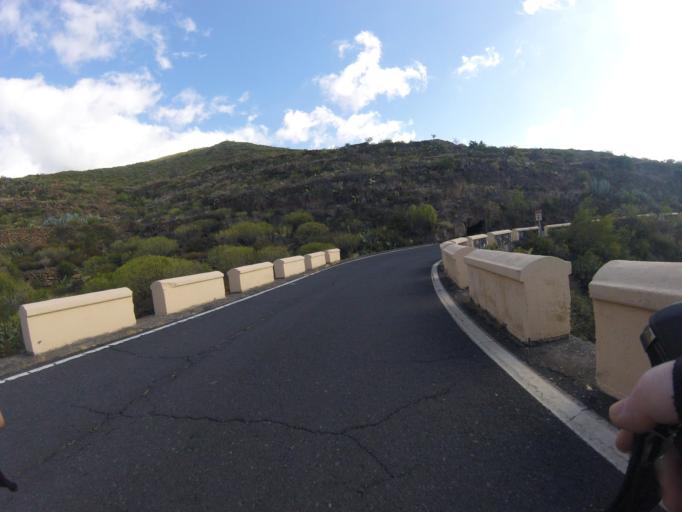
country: ES
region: Canary Islands
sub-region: Provincia de Santa Cruz de Tenerife
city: Candelaria
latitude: 28.4051
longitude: -16.3480
